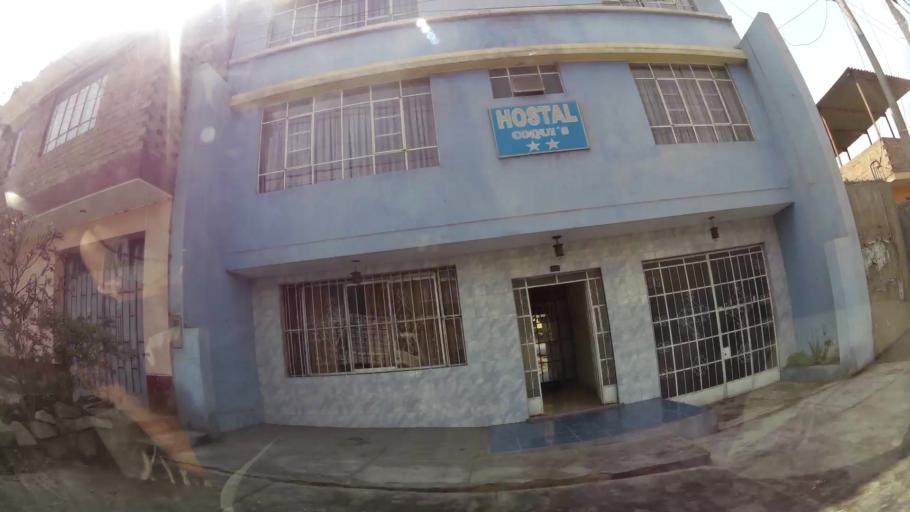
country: PE
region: Lima
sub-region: Lima
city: Asentamiento Humano Nicolas de Pierola
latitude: -11.9382
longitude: -76.7009
